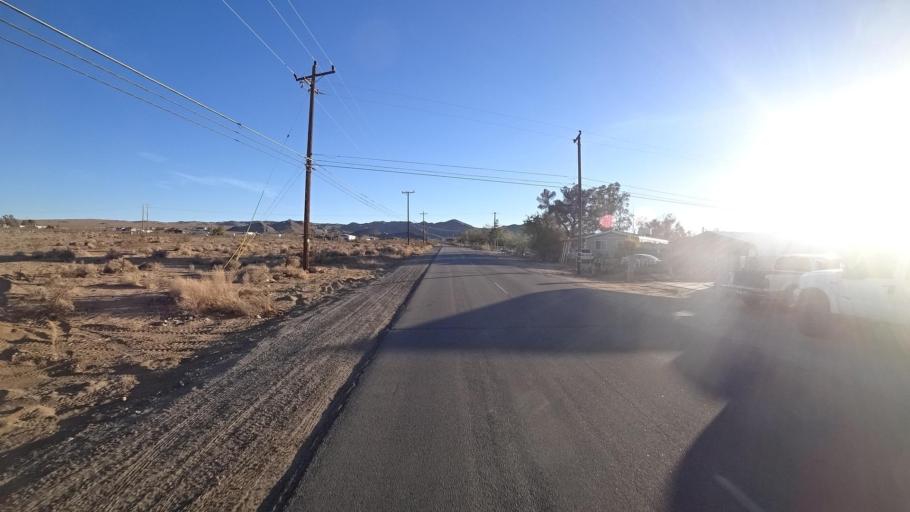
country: US
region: California
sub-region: Kern County
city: Ridgecrest
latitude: 35.5948
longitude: -117.6528
